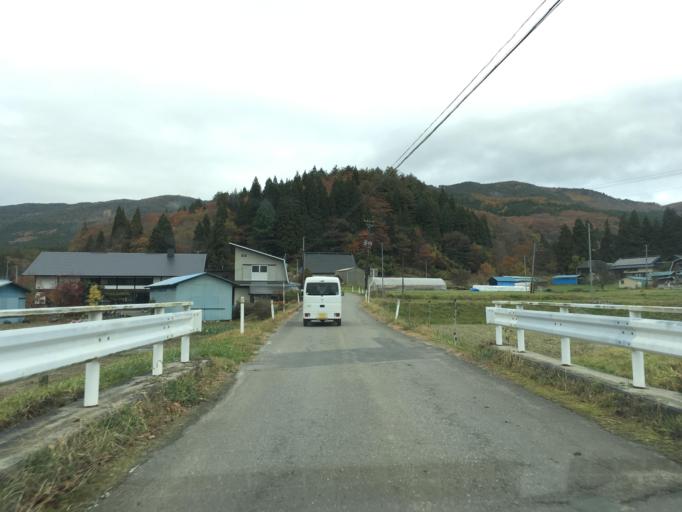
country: JP
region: Iwate
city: Mizusawa
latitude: 39.1118
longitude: 141.3275
